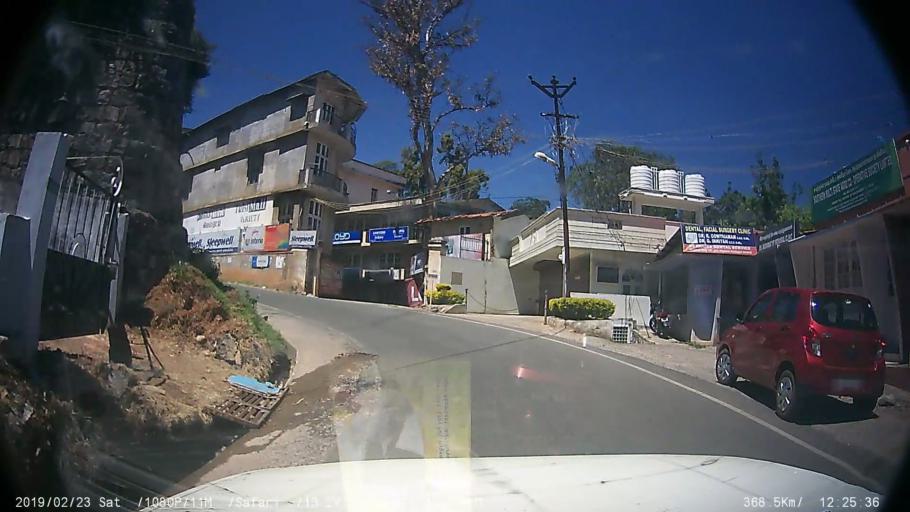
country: IN
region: Tamil Nadu
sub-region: Nilgiri
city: Wellington
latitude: 11.3424
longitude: 76.7899
